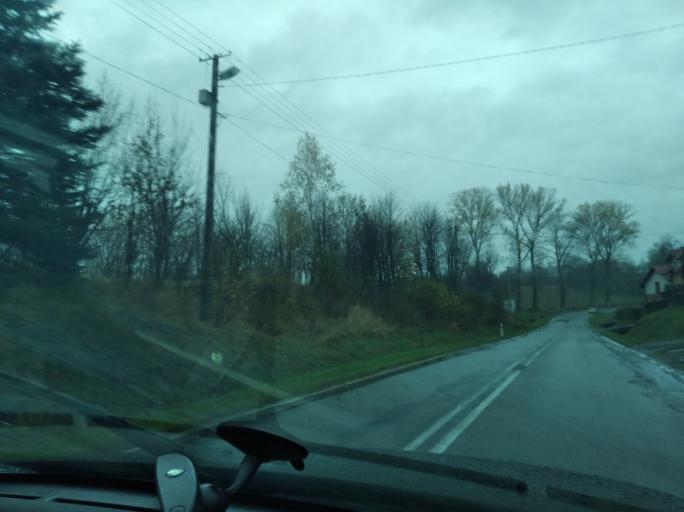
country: PL
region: Subcarpathian Voivodeship
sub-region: Powiat lancucki
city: Albigowa
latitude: 50.0080
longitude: 22.2150
